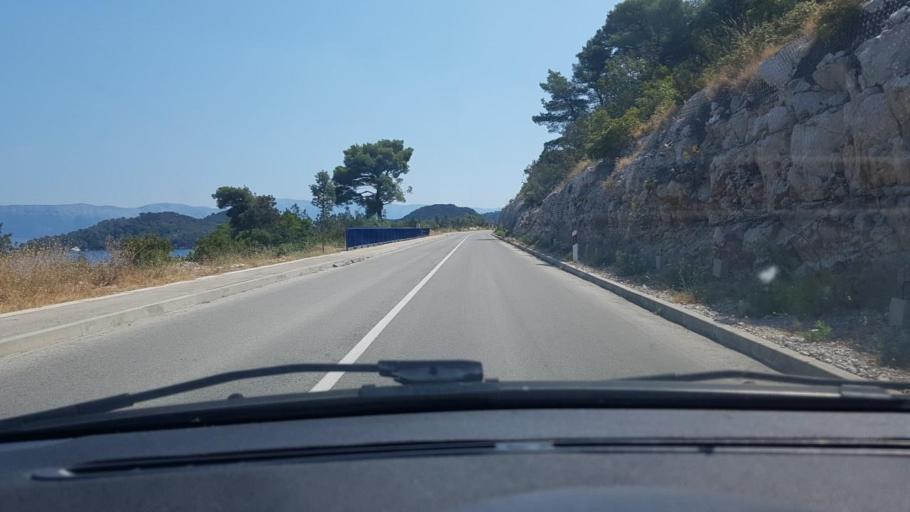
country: HR
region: Dubrovacko-Neretvanska
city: Blato
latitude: 42.7866
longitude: 17.3829
